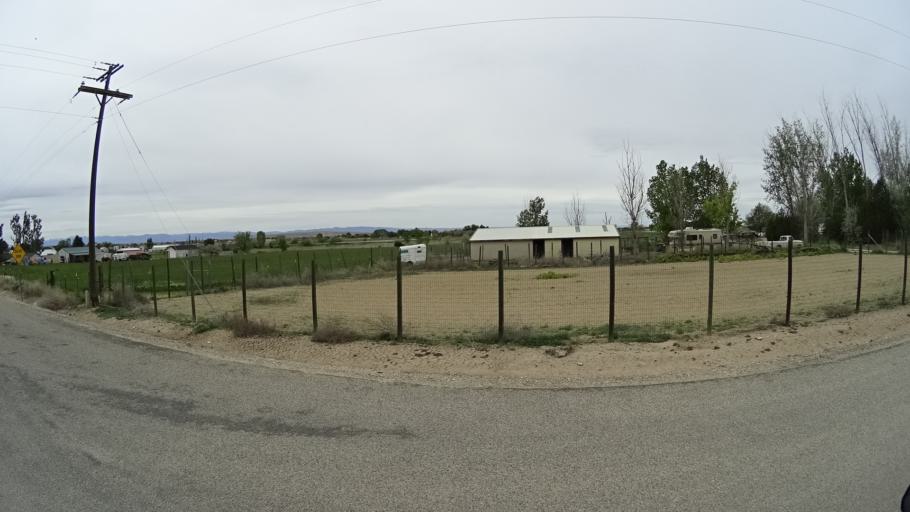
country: US
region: Idaho
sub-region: Ada County
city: Kuna
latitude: 43.4938
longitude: -116.3394
